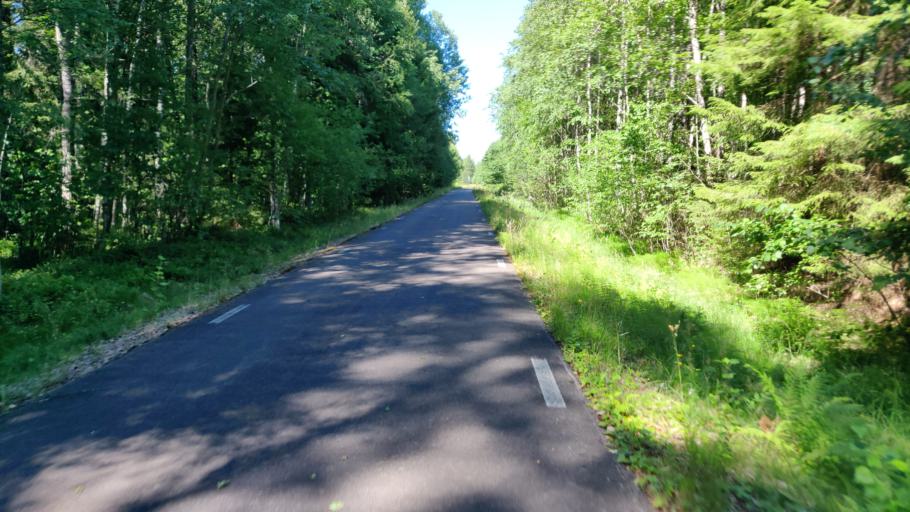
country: SE
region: Vaermland
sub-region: Hagfors Kommun
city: Hagfors
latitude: 59.9643
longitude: 13.5722
